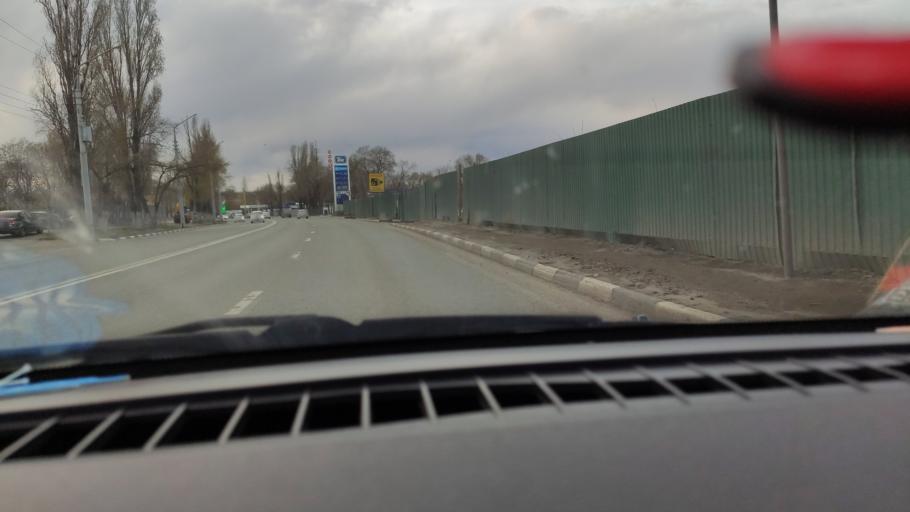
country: RU
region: Saratov
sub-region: Saratovskiy Rayon
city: Saratov
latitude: 51.5799
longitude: 45.9817
